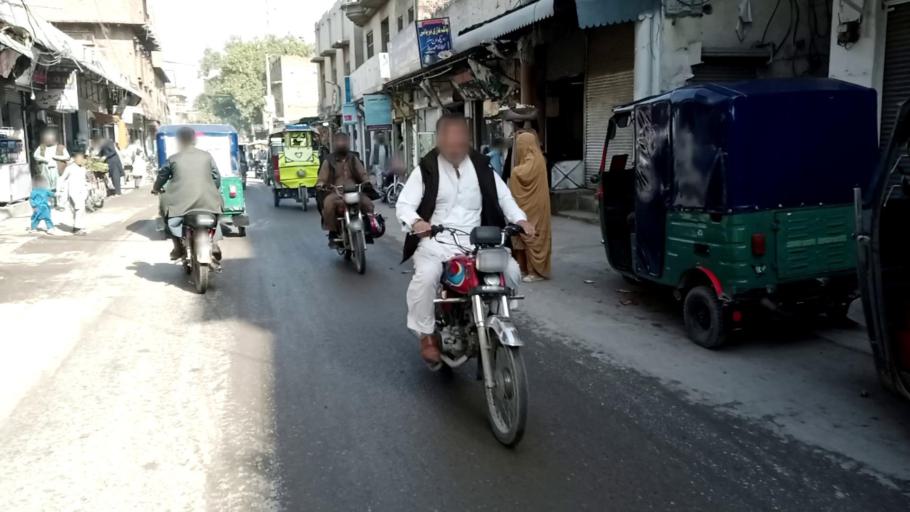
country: PK
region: Khyber Pakhtunkhwa
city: Peshawar
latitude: 33.9987
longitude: 71.5786
